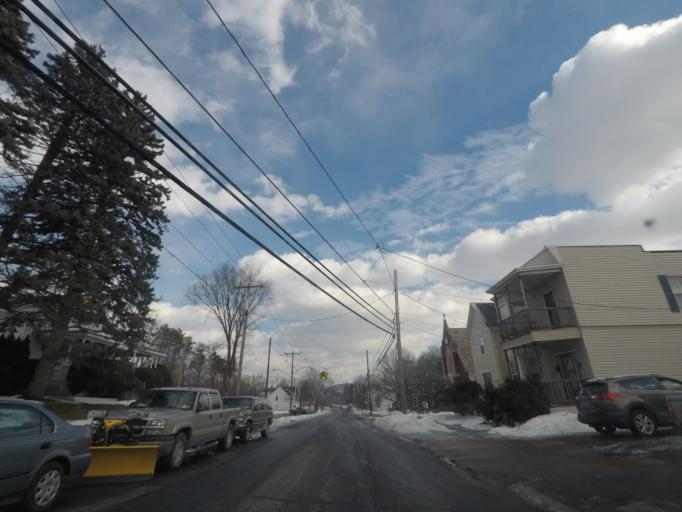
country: US
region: New York
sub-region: Albany County
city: Cohoes
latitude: 42.7779
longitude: -73.7138
